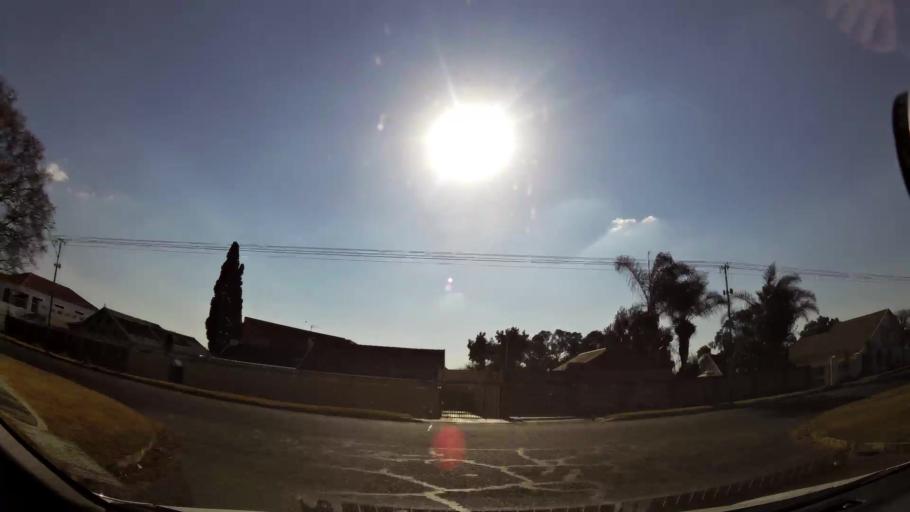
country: ZA
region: Gauteng
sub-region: City of Johannesburg Metropolitan Municipality
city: Johannesburg
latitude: -26.2548
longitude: 27.9958
